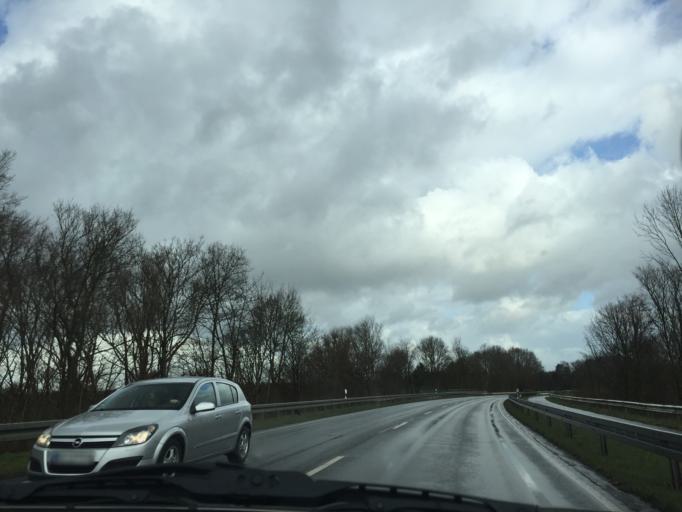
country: DE
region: North Rhine-Westphalia
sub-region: Regierungsbezirk Dusseldorf
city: Emmerich
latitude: 51.8410
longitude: 6.2270
